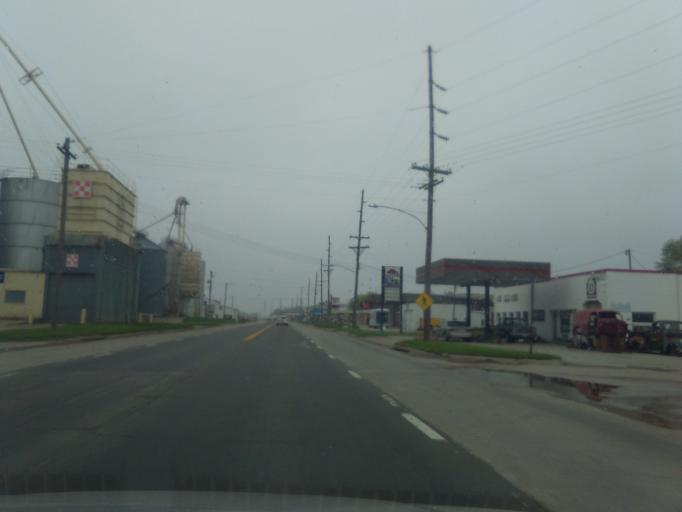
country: US
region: Nebraska
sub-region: Cuming County
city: Wisner
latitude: 41.9278
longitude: -96.8105
